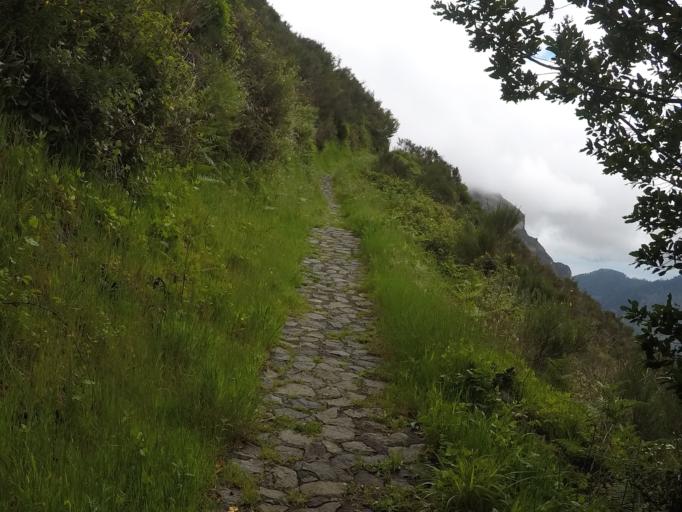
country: PT
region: Madeira
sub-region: Camara de Lobos
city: Curral das Freiras
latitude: 32.7355
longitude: -16.9999
